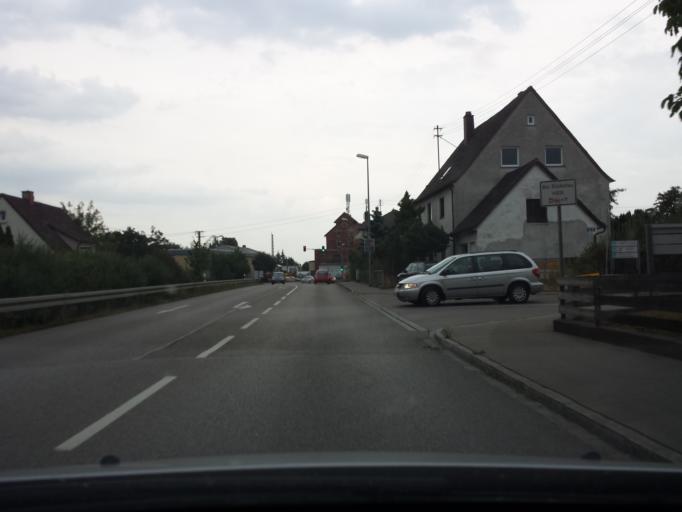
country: DE
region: Bavaria
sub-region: Swabia
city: Nersingen
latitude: 48.4279
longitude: 10.1202
